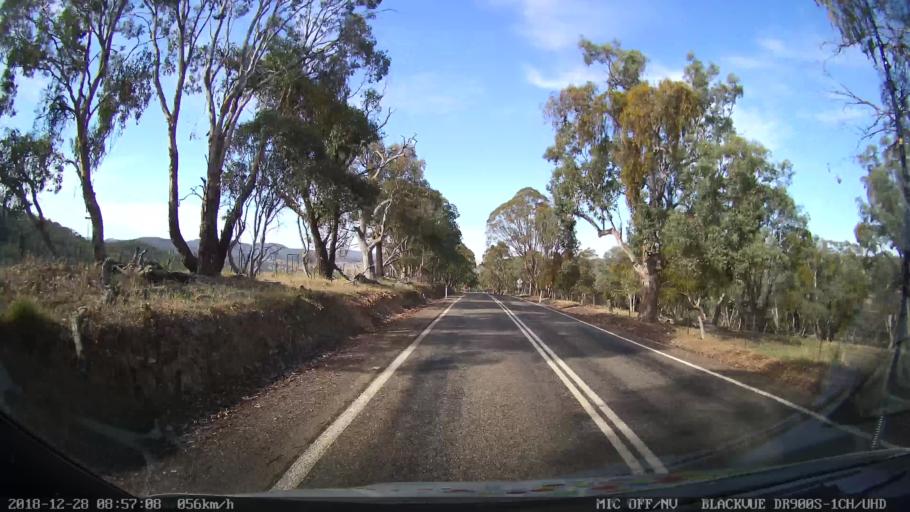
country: AU
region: New South Wales
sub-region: Upper Lachlan Shire
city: Crookwell
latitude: -34.1166
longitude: 149.3373
